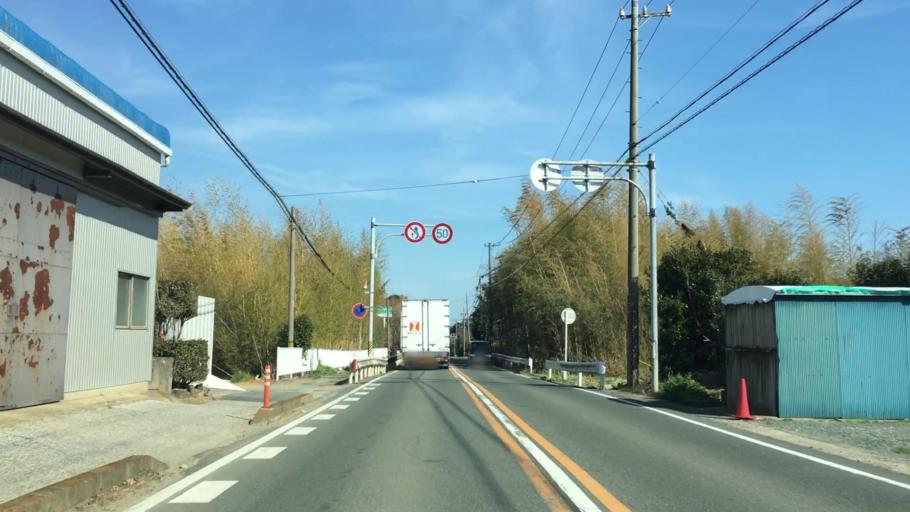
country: JP
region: Shizuoka
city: Kosai-shi
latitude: 34.6842
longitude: 137.4599
